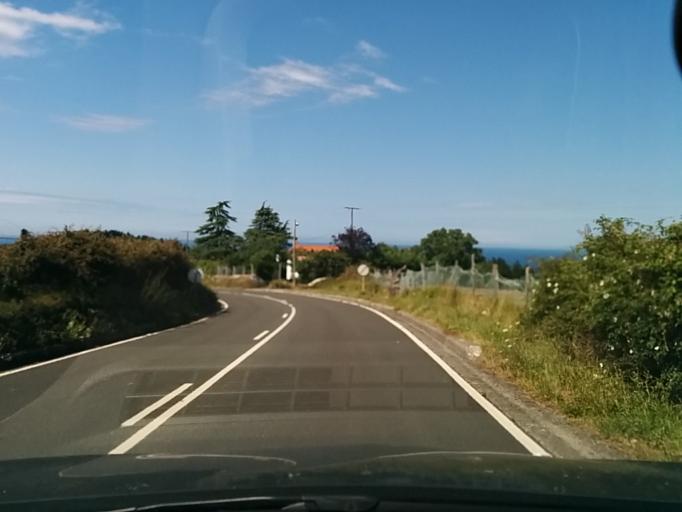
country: ES
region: Basque Country
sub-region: Bizkaia
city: Mendexa
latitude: 43.3496
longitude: -2.4895
